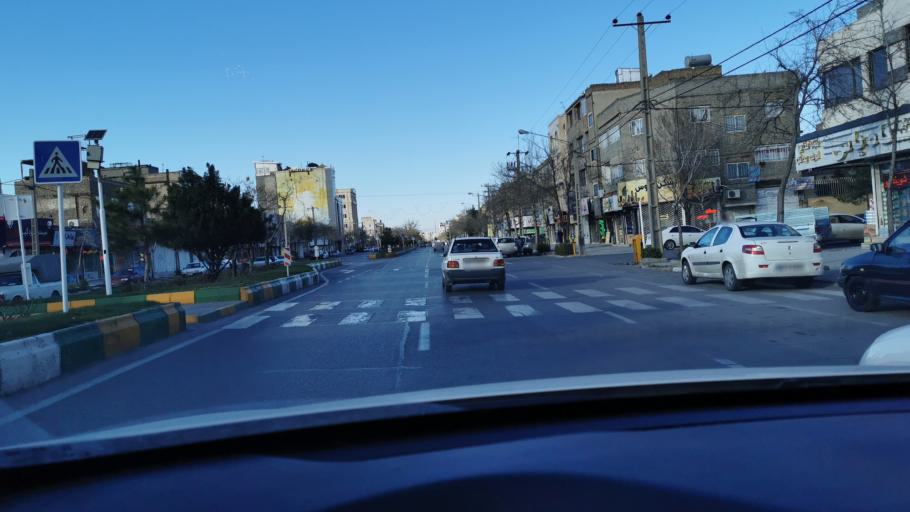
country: IR
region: Razavi Khorasan
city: Mashhad
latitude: 36.3331
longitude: 59.5209
